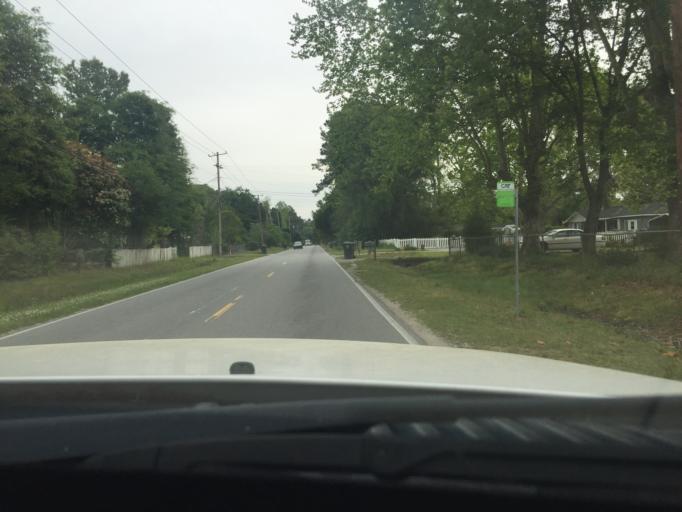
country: US
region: Georgia
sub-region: Chatham County
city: Georgetown
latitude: 31.9865
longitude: -81.2570
